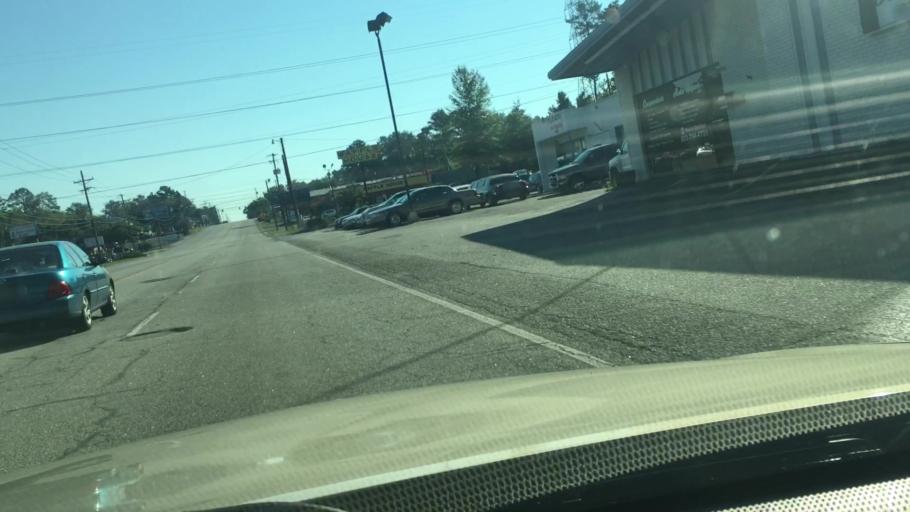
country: US
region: South Carolina
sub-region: Lexington County
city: Cayce
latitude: 33.9599
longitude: -81.0892
